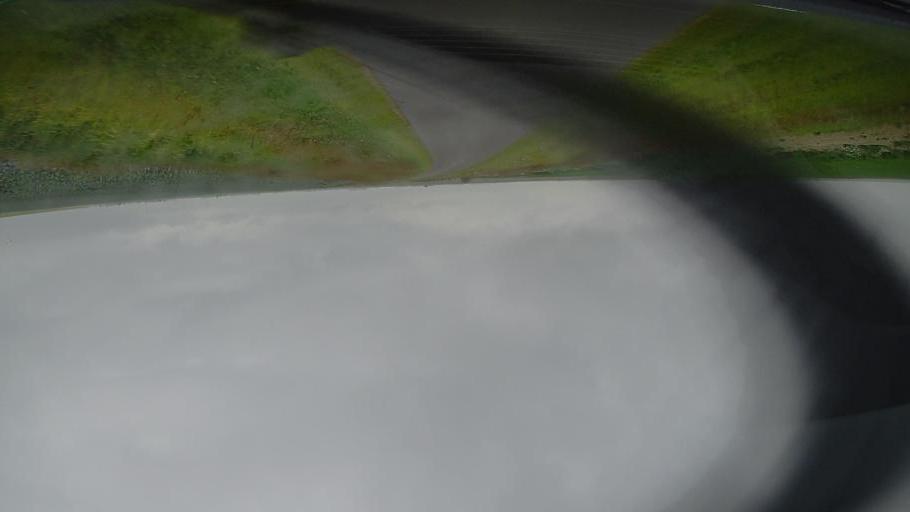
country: DE
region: Schleswig-Holstein
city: Friedrichsgabekoog
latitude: 54.1057
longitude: 8.9883
